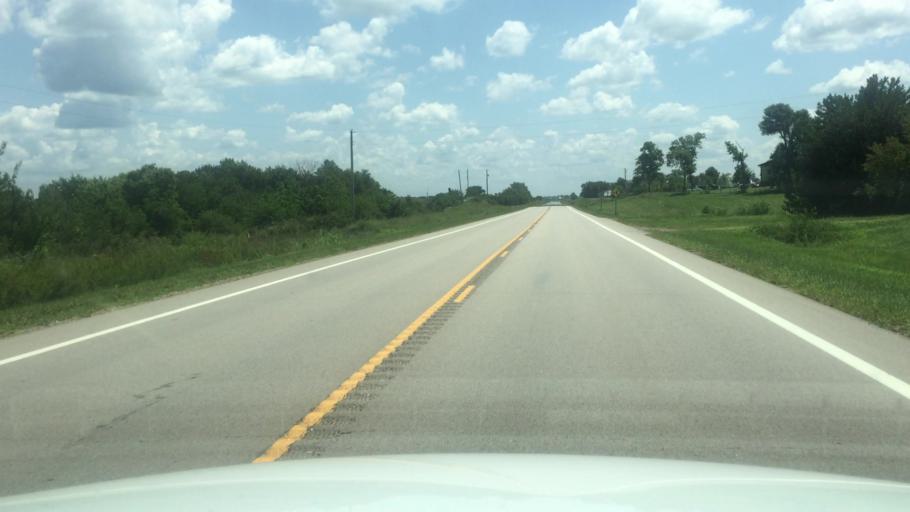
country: US
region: Kansas
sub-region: Brown County
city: Horton
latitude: 39.6074
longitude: -95.3423
